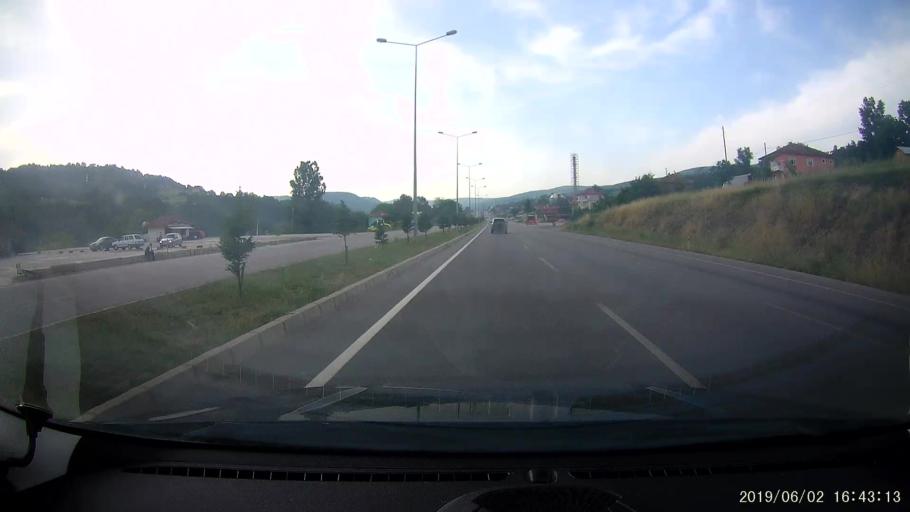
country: TR
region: Samsun
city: Kavak
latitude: 41.1316
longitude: 36.1317
